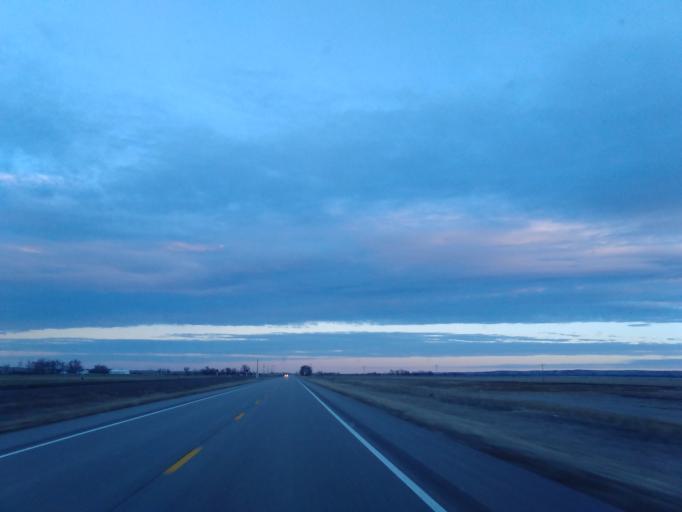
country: US
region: Nebraska
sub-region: Garden County
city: Oshkosh
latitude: 41.3969
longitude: -102.3177
